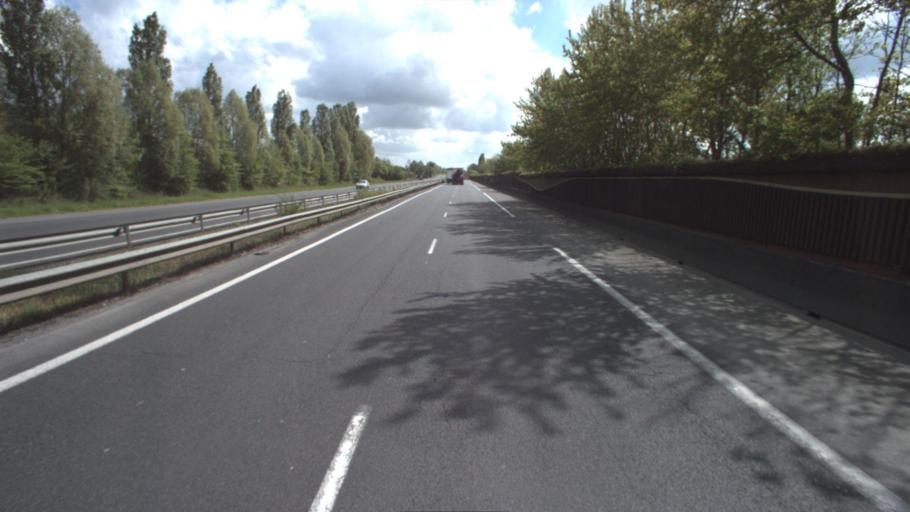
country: FR
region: Ile-de-France
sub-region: Departement de Seine-et-Marne
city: Fontenay-Tresigny
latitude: 48.7126
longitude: 2.8609
